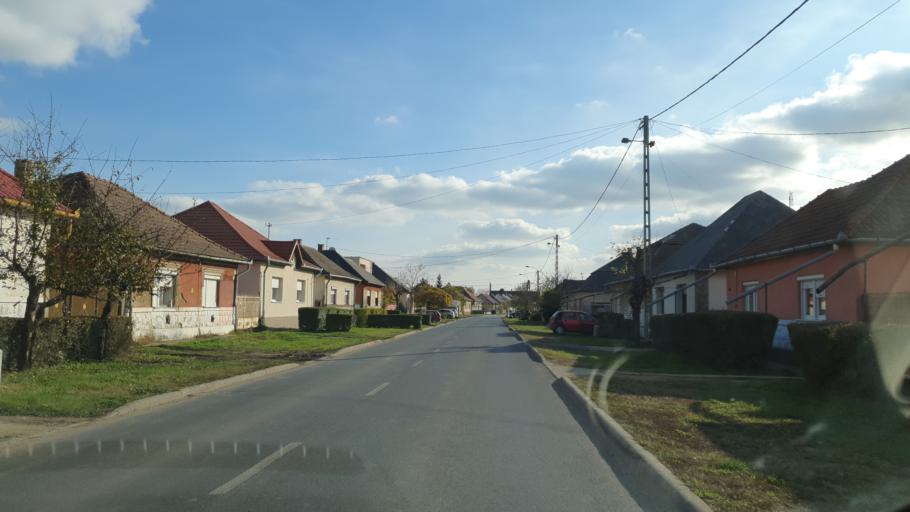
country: HU
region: Szabolcs-Szatmar-Bereg
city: Kisvarda
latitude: 48.2205
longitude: 22.0769
